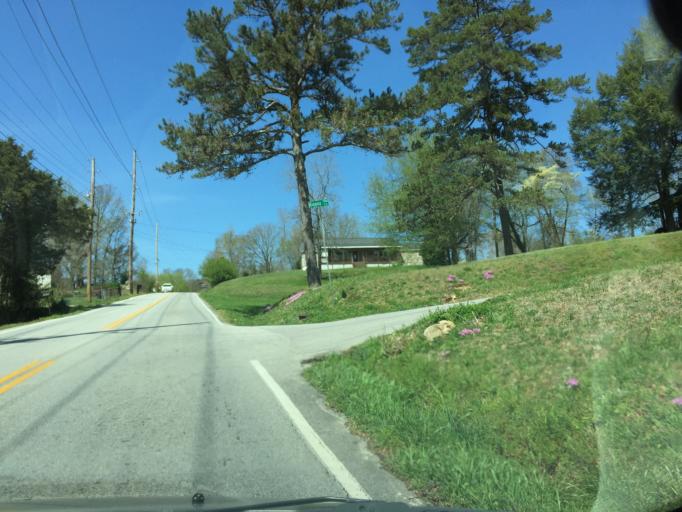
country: US
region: Tennessee
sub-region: Hamilton County
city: Middle Valley
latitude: 35.1952
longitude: -85.1967
